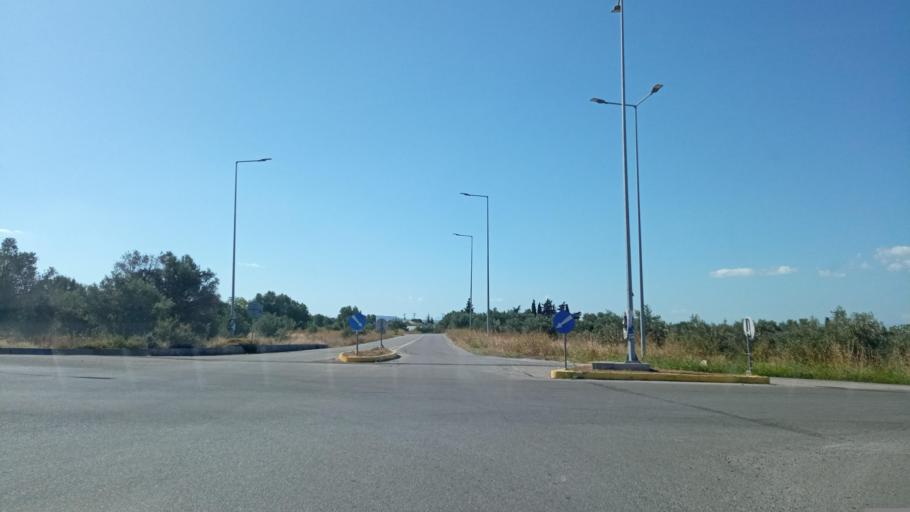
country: GR
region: Central Greece
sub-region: Nomos Evvoias
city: Psachna
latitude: 38.5801
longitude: 23.7686
